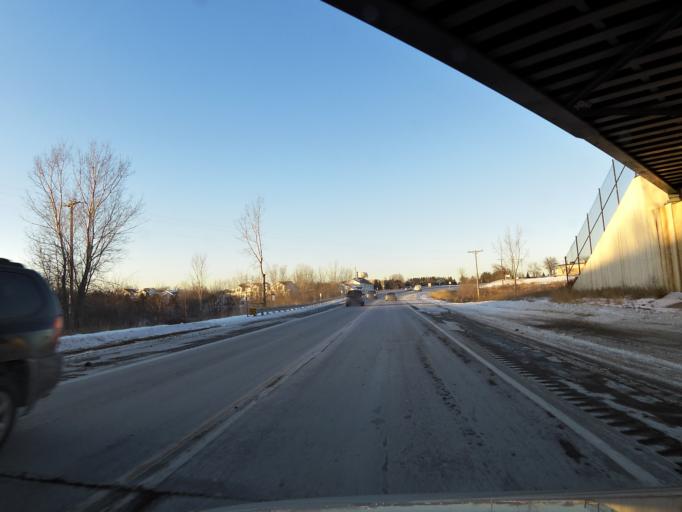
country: US
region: Minnesota
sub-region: Dakota County
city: Rosemount
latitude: 44.7242
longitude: -93.1320
